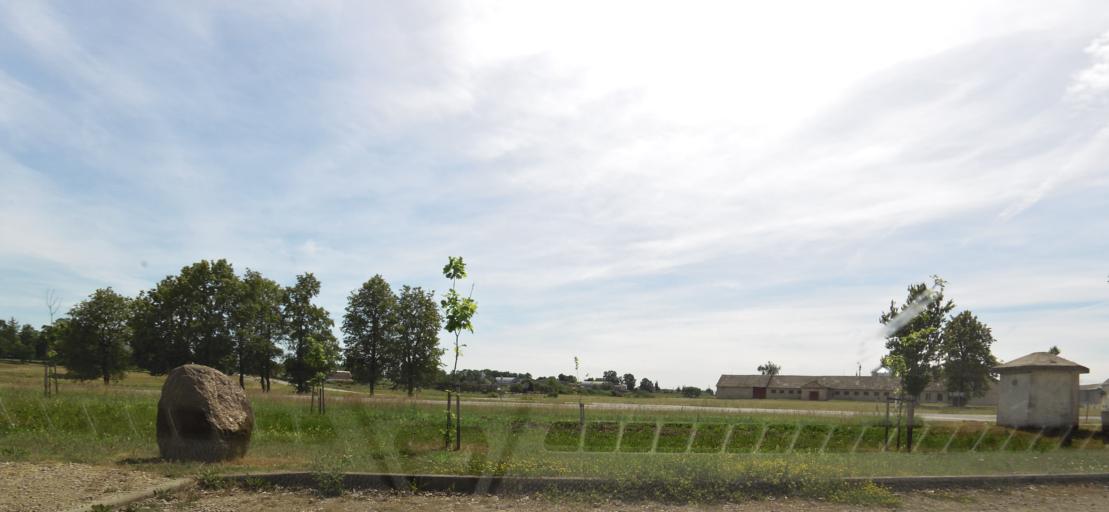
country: LT
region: Panevezys
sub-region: Panevezys City
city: Panevezys
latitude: 55.6542
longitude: 24.2228
